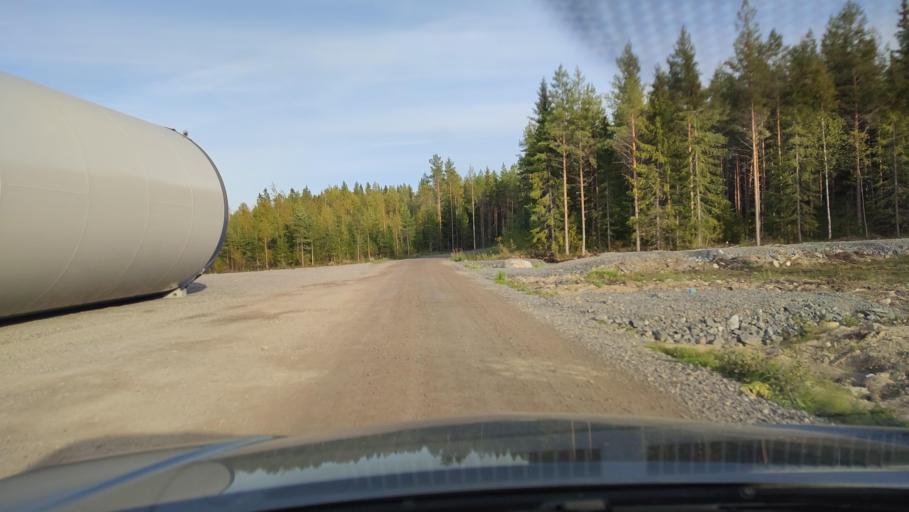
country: FI
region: Southern Ostrobothnia
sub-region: Suupohja
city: Karijoki
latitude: 62.1671
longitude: 21.6042
